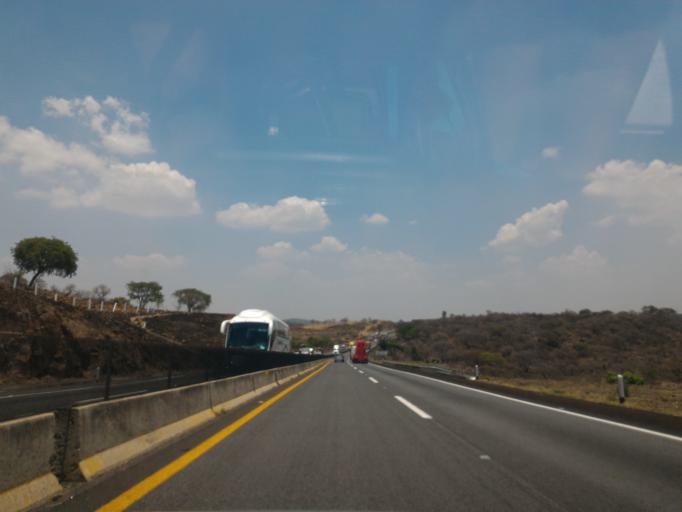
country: MX
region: Jalisco
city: Zapotlanejo
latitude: 20.6624
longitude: -103.0475
